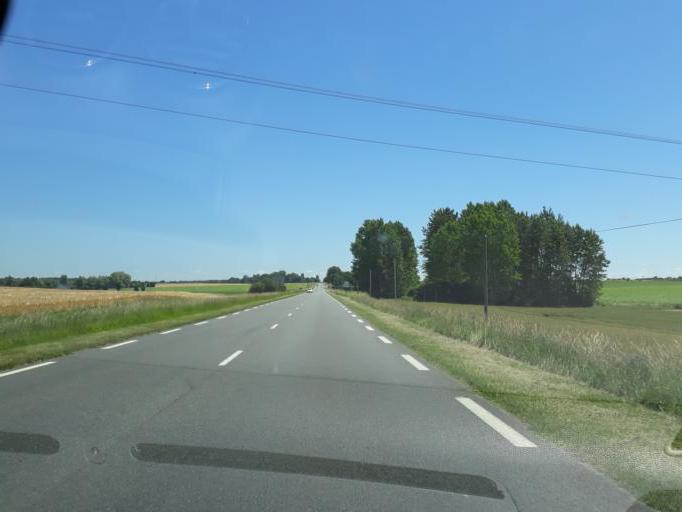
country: FR
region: Centre
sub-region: Departement du Cher
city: Marmagne
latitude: 47.1378
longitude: 2.2658
